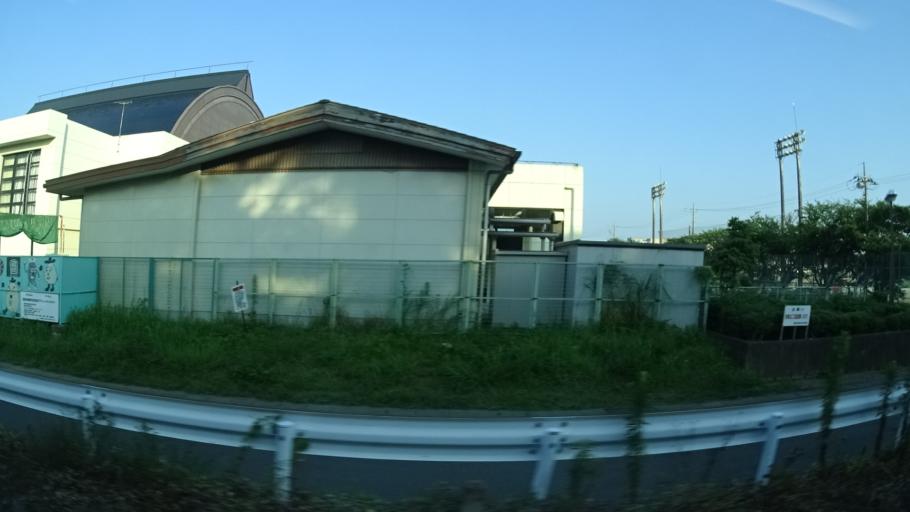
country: JP
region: Ibaraki
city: Funaishikawa
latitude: 36.4605
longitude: 140.5596
